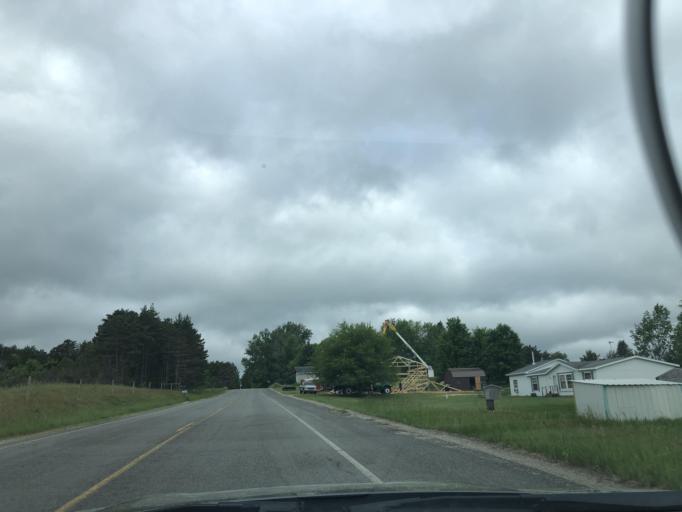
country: US
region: Michigan
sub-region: Missaukee County
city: Lake City
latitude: 44.4538
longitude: -85.2133
